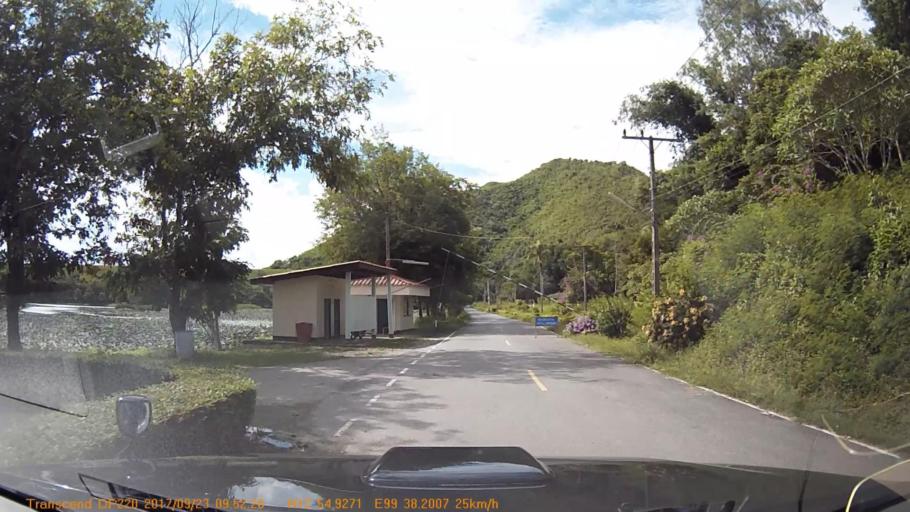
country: TH
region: Phetchaburi
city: Kaeng Krachan
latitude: 12.9158
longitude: 99.6363
